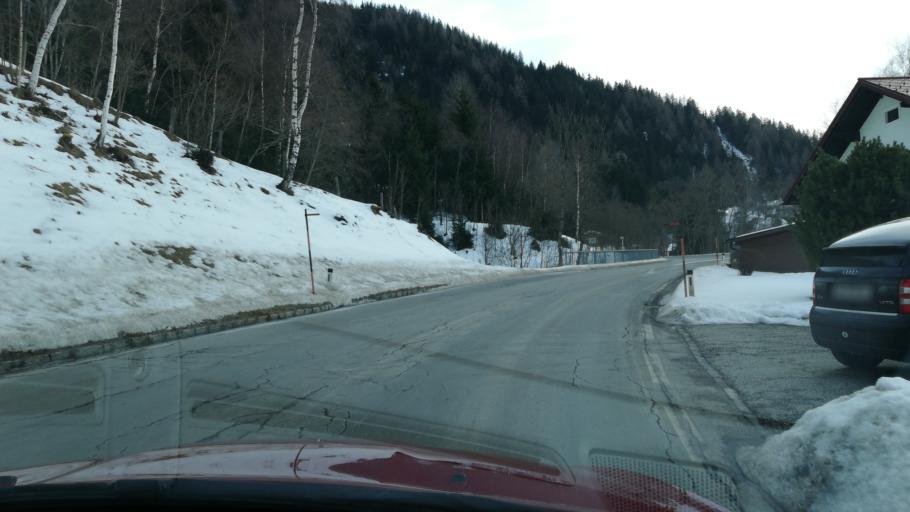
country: AT
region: Styria
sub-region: Politischer Bezirk Liezen
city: Donnersbach
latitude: 47.4484
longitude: 14.1432
